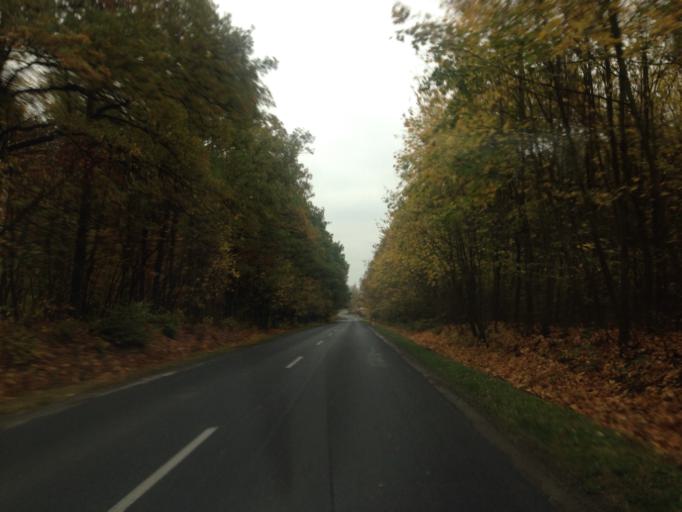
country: PL
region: Kujawsko-Pomorskie
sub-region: Powiat brodnicki
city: Brodnica
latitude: 53.2612
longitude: 19.3426
